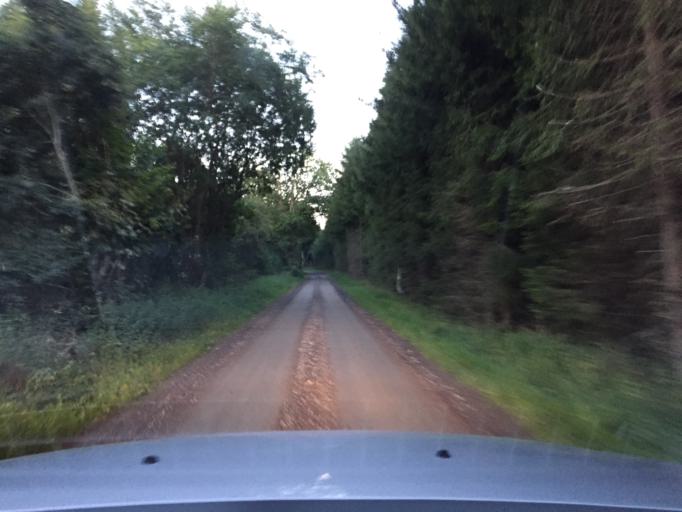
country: SE
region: Skane
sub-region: Hassleholms Kommun
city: Sosdala
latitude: 55.9879
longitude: 13.6756
